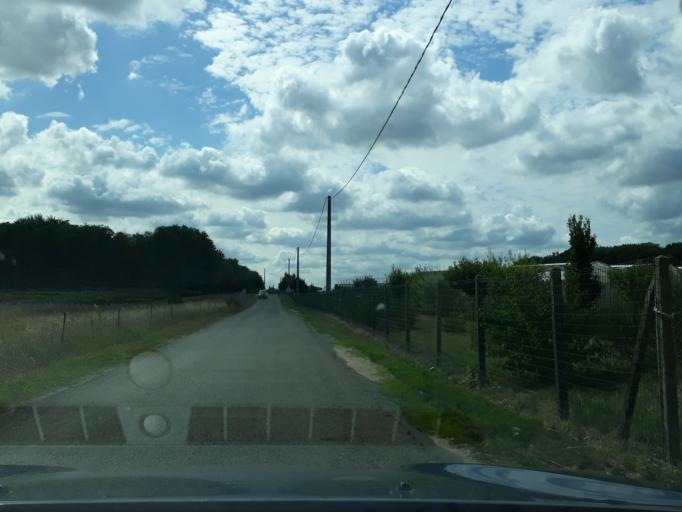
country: FR
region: Centre
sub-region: Departement du Loiret
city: Saint-Cyr-en-Val
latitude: 47.8524
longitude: 1.9770
